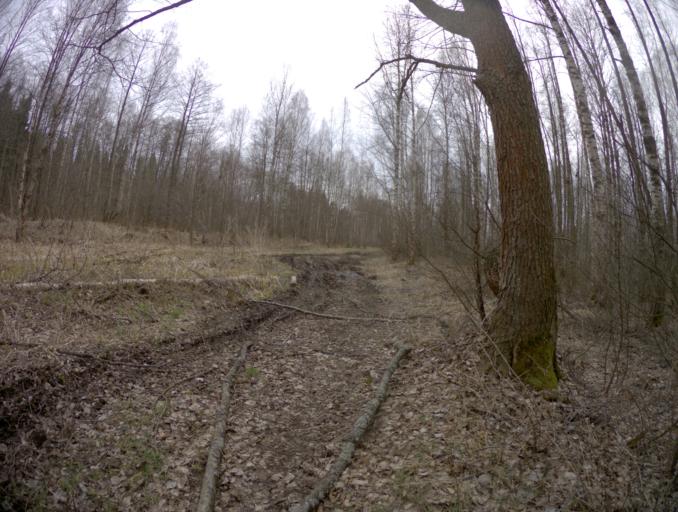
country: RU
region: Vladimir
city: Raduzhnyy
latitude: 55.9185
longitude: 40.2450
